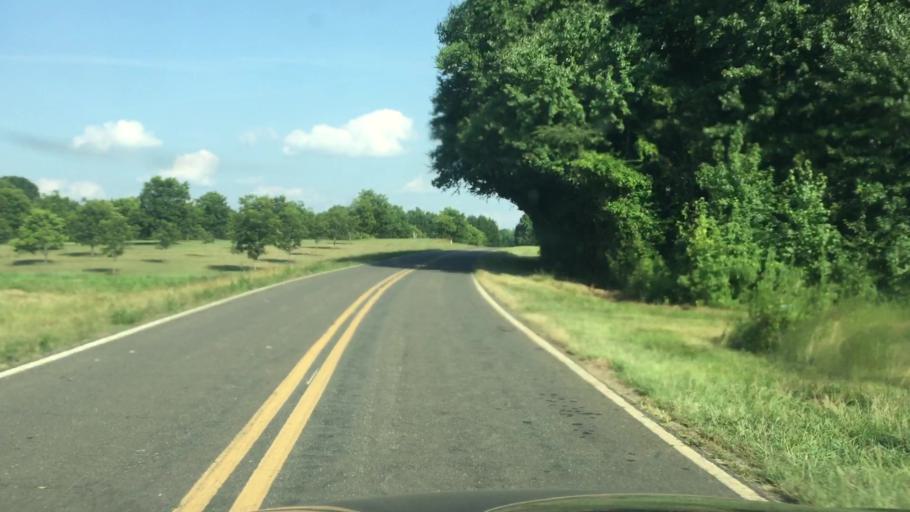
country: US
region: North Carolina
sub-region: Rockingham County
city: Reidsville
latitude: 36.2773
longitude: -79.5888
